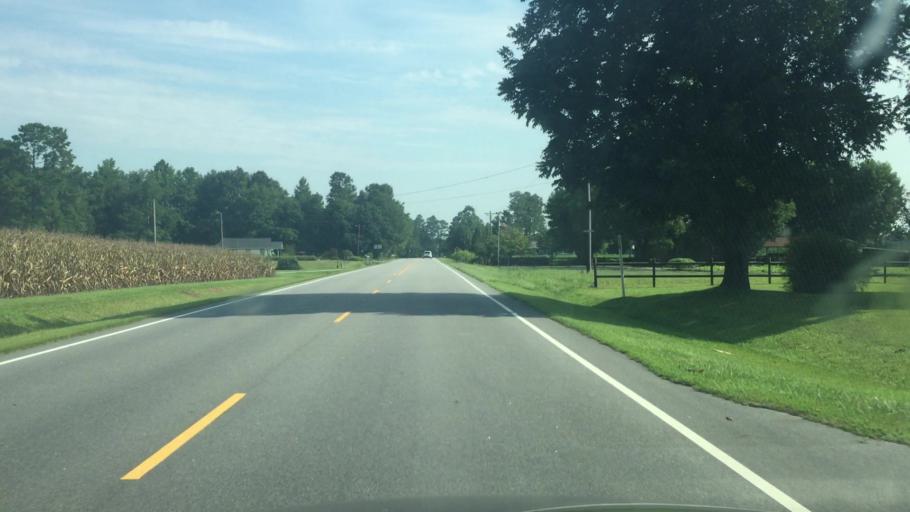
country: US
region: North Carolina
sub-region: Columbus County
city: Chadbourn
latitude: 34.2442
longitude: -78.8207
